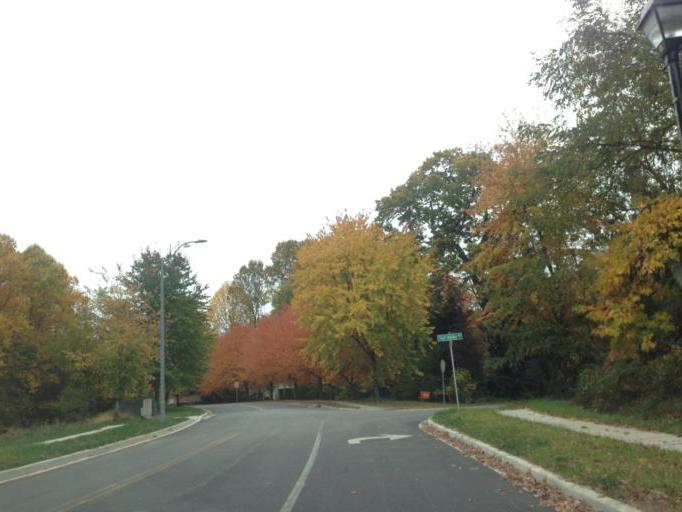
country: US
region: Maryland
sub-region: Howard County
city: Columbia
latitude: 39.3010
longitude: -76.8776
